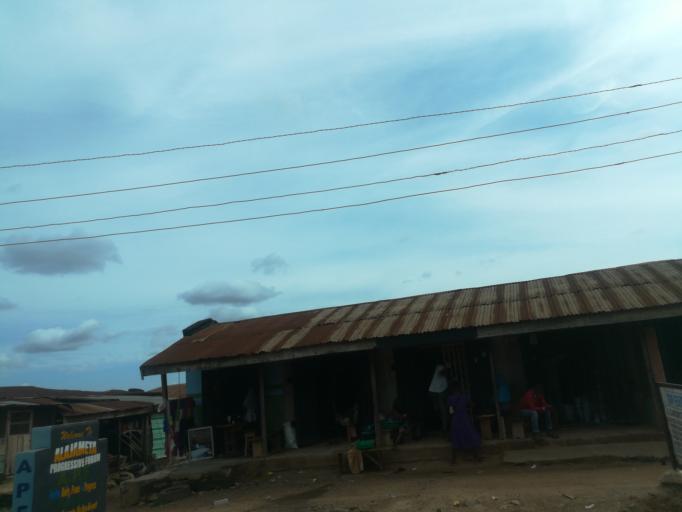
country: NG
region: Oyo
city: Ibadan
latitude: 7.3770
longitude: 3.9599
